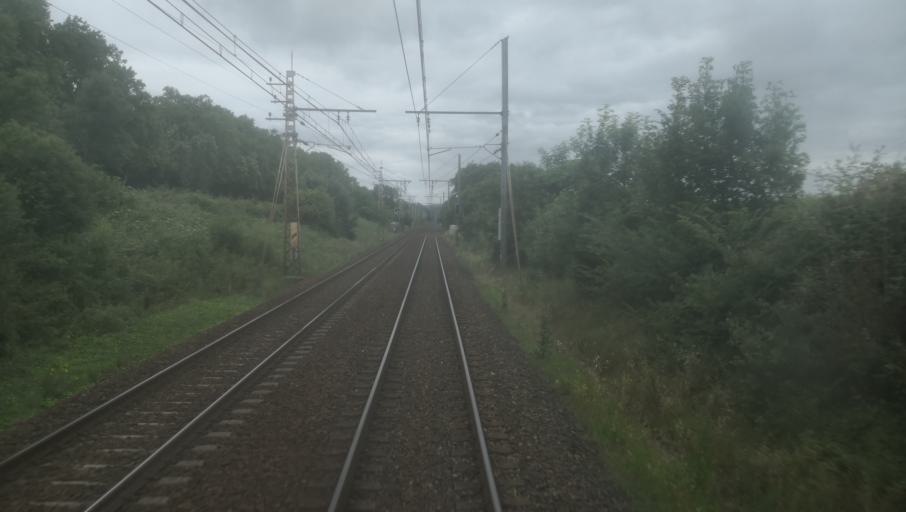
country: FR
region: Midi-Pyrenees
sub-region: Departement de la Haute-Garonne
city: Saint-Jory
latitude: 43.7548
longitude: 1.3613
